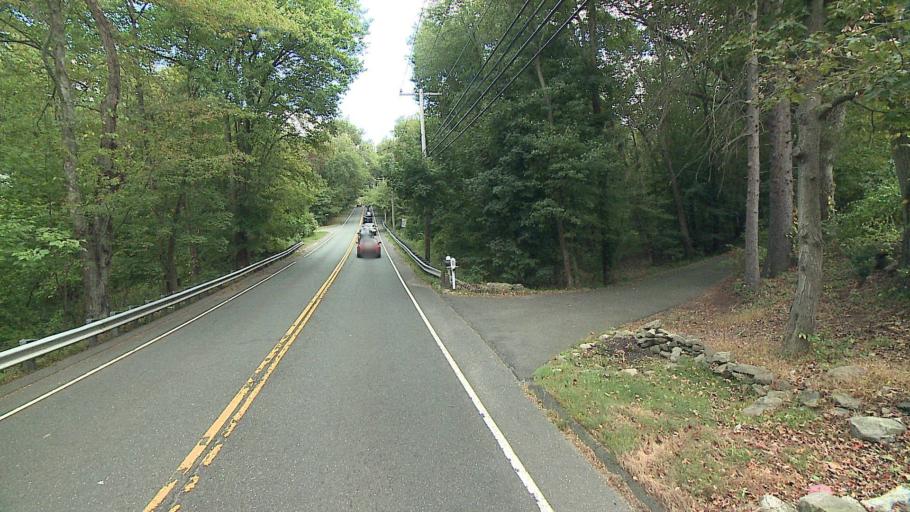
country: US
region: Connecticut
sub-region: Fairfield County
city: Wilton
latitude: 41.1769
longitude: -73.3982
